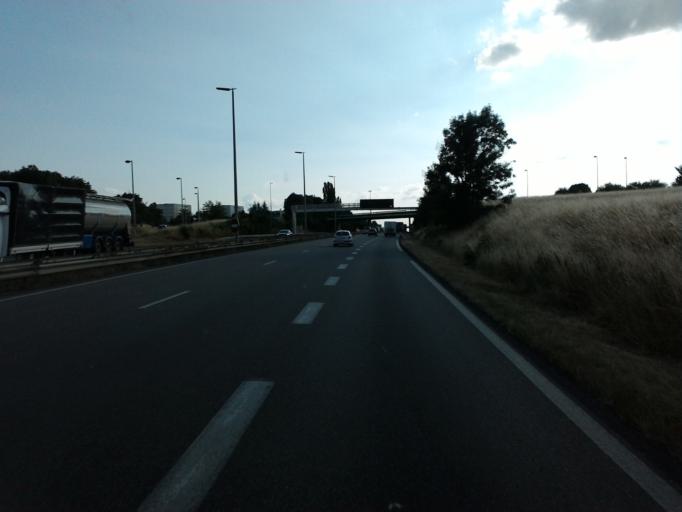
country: FR
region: Lorraine
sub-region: Departement de Meurthe-et-Moselle
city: Laxou
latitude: 48.7055
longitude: 6.1375
